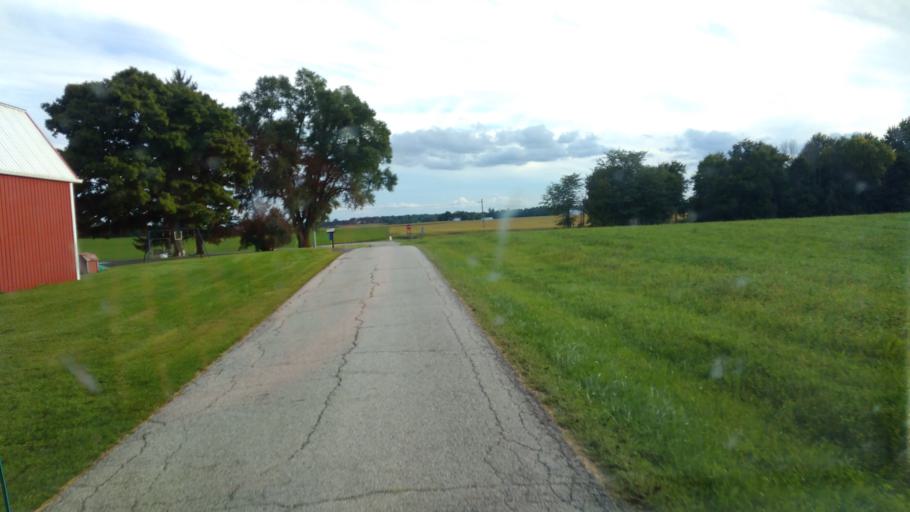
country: US
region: Ohio
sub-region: Crawford County
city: Bucyrus
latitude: 40.8505
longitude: -82.9163
